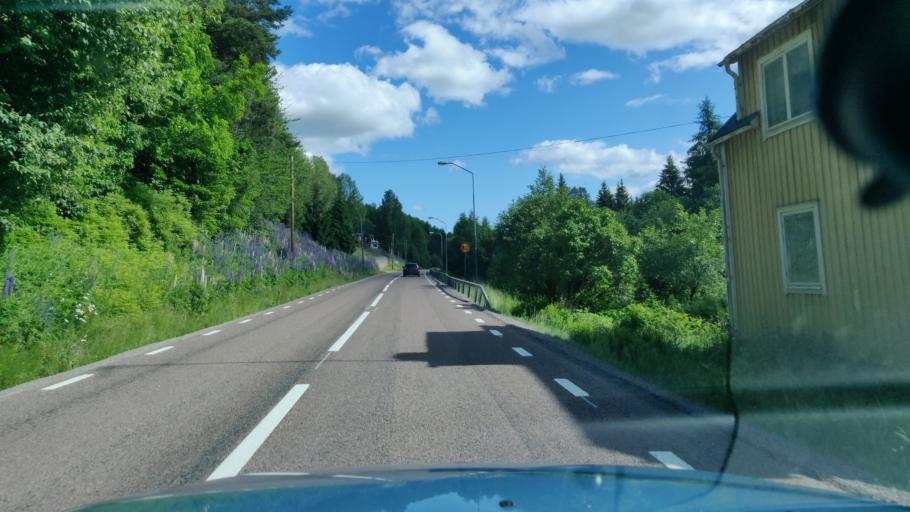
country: SE
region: Vaermland
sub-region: Torsby Kommun
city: Torsby
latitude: 60.6447
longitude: 13.0035
